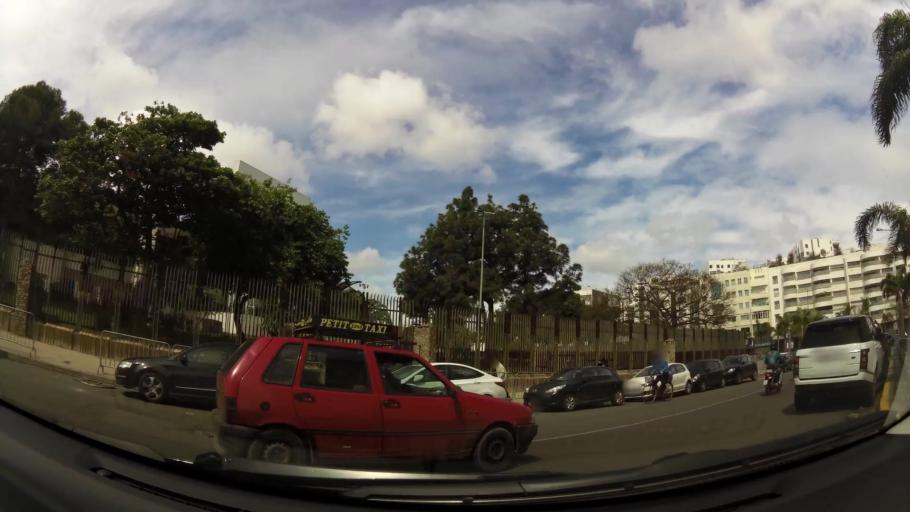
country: MA
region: Grand Casablanca
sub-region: Casablanca
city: Casablanca
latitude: 33.5842
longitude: -7.6455
